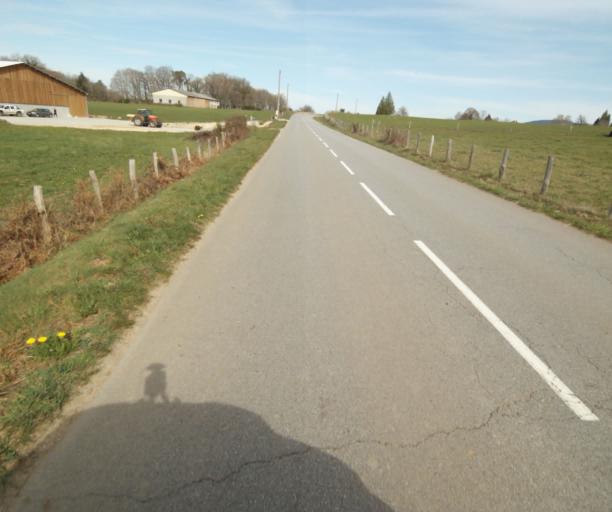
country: FR
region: Limousin
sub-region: Departement de la Correze
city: Correze
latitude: 45.3996
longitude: 1.8266
